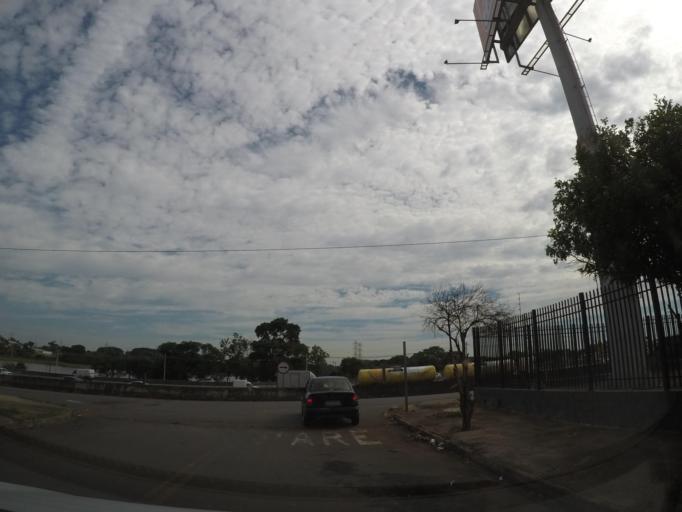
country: BR
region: Sao Paulo
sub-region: Hortolandia
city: Hortolandia
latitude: -22.8268
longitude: -47.1863
